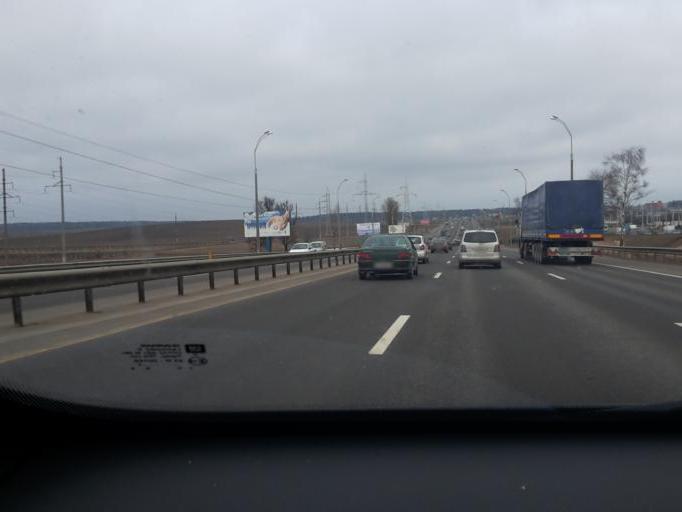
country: BY
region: Minsk
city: Novoye Medvezhino
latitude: 53.8871
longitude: 27.4144
